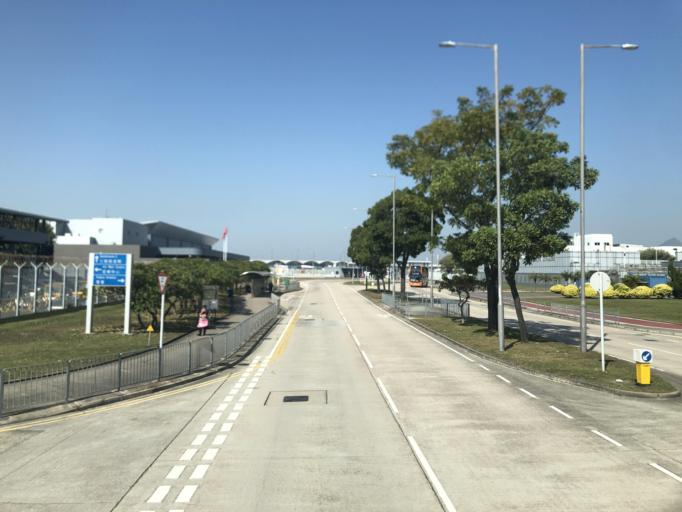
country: HK
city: Tai O
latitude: 22.3013
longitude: 113.9312
